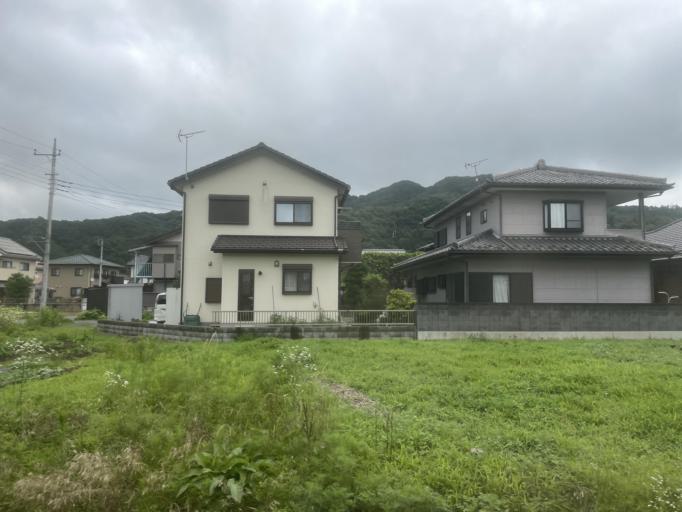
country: JP
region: Saitama
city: Yorii
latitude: 36.0827
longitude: 139.1152
